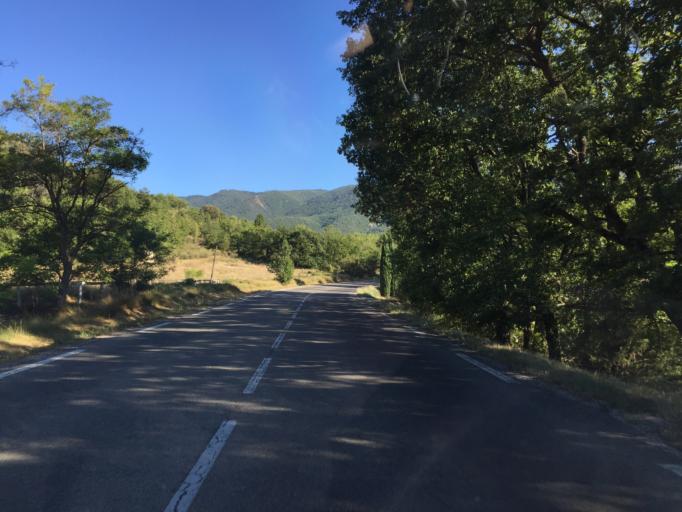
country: FR
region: Provence-Alpes-Cote d'Azur
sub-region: Departement du Vaucluse
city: Saignon
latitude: 43.8558
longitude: 5.4768
